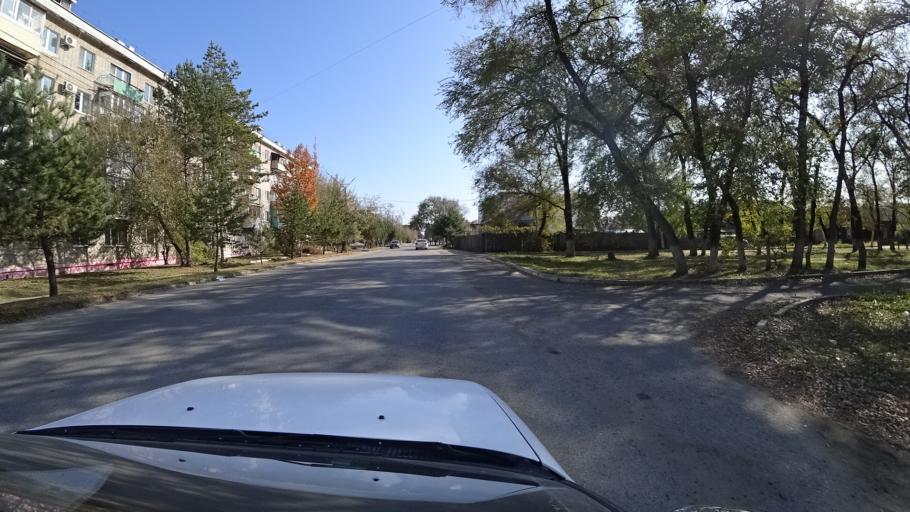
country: RU
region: Primorskiy
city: Dal'nerechensk
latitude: 45.9348
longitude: 133.7282
